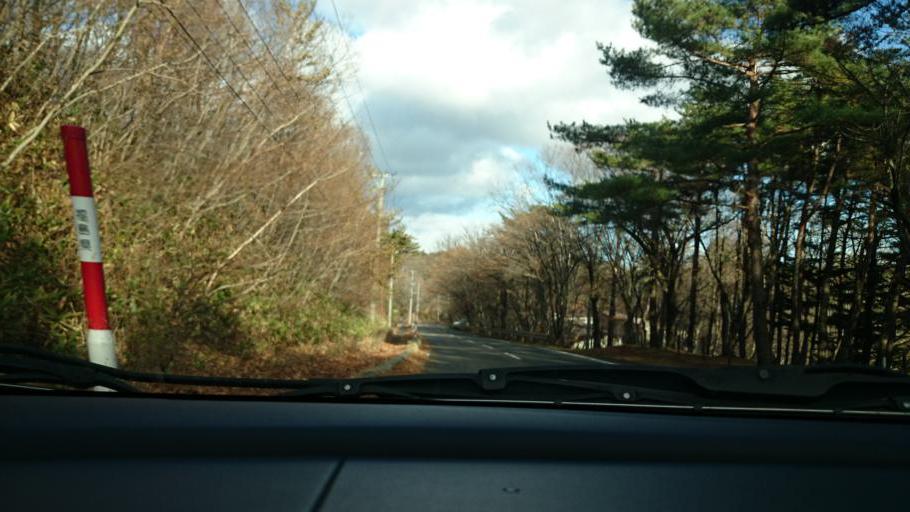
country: JP
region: Tochigi
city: Kuroiso
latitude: 37.1734
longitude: 140.0378
